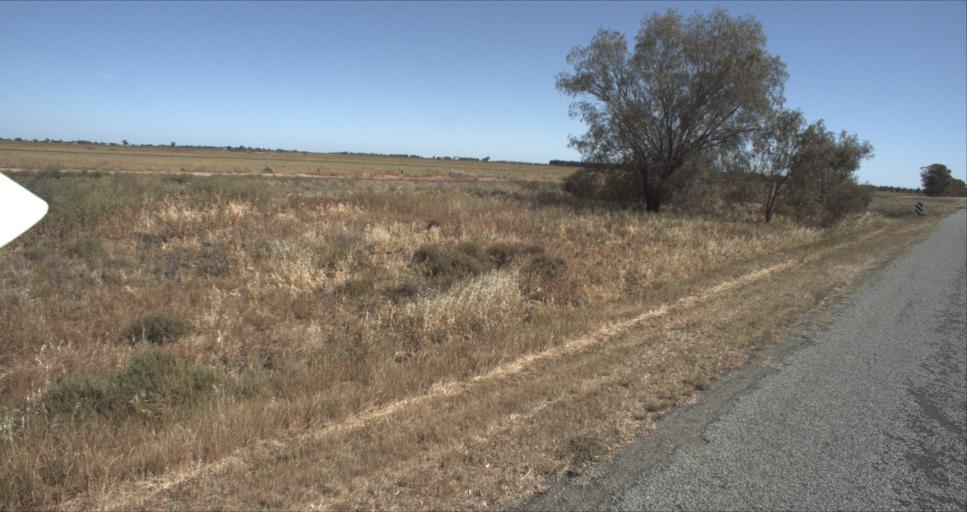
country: AU
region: New South Wales
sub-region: Leeton
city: Leeton
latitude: -34.5402
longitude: 146.3166
